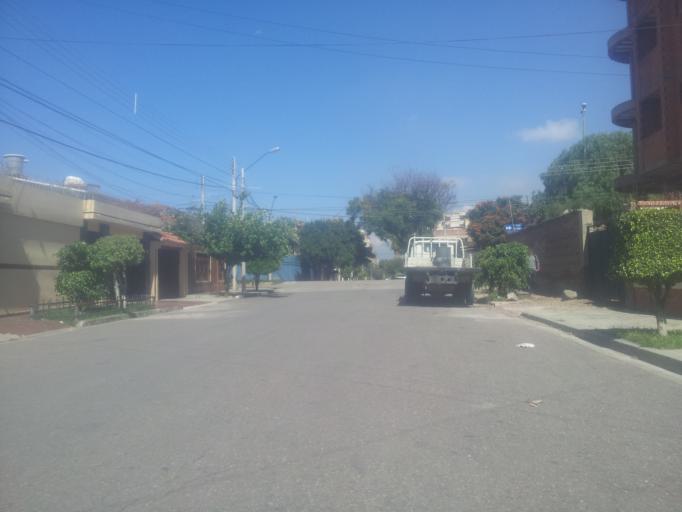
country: BO
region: Cochabamba
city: Cochabamba
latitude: -17.3781
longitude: -66.1728
